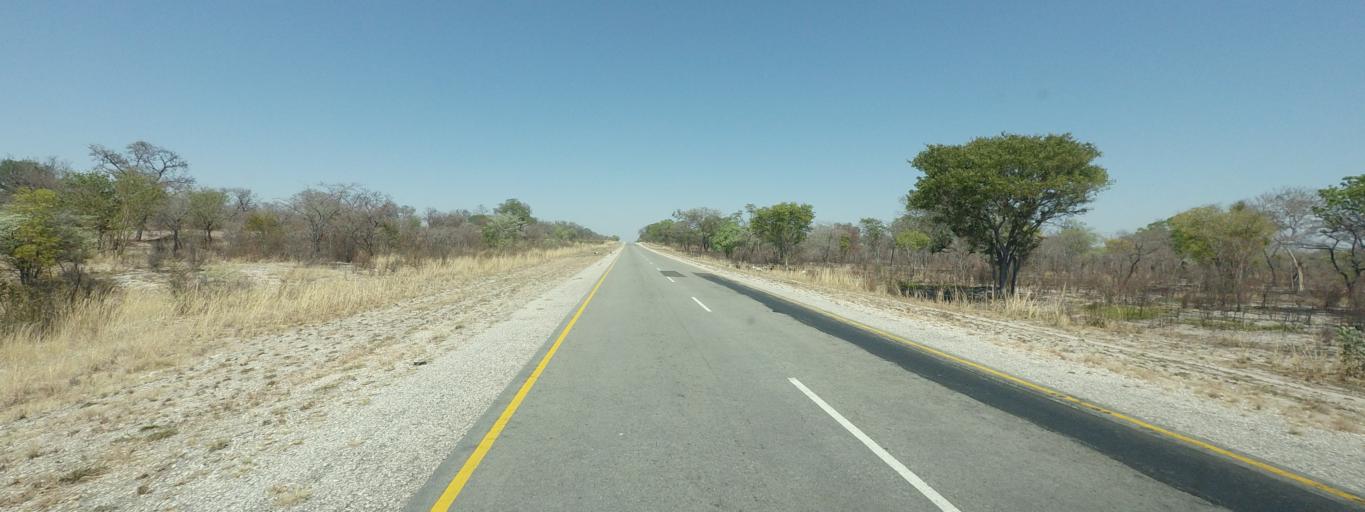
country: BW
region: North West
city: Shakawe
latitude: -17.9503
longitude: 22.5899
